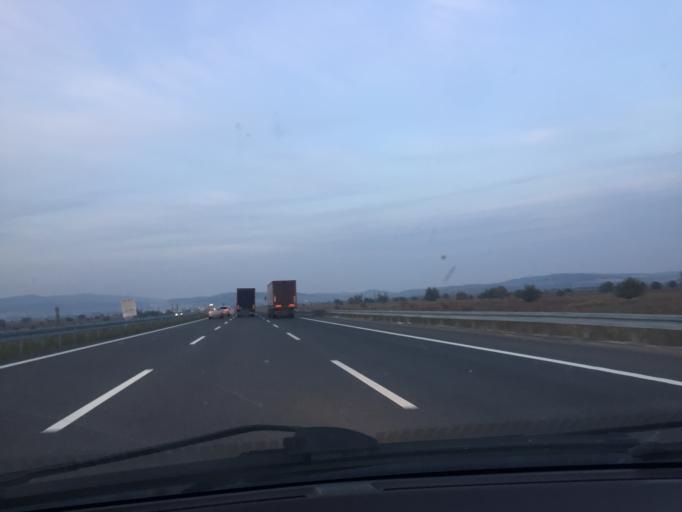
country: TR
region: Manisa
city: Halitpasa
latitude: 38.7477
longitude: 27.6596
